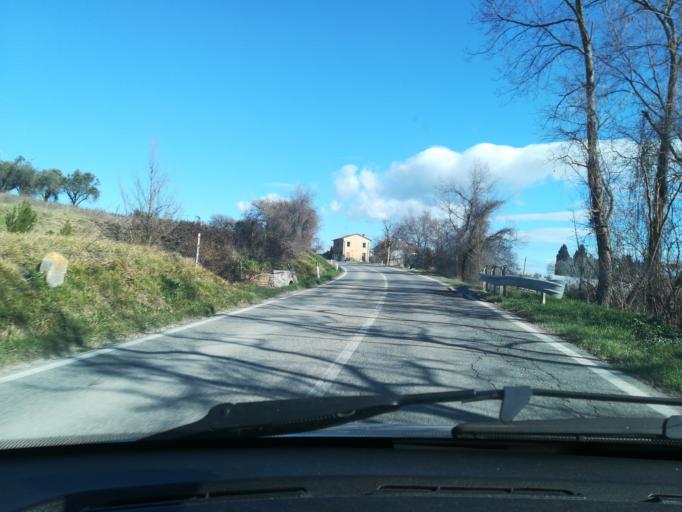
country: IT
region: The Marches
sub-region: Provincia di Macerata
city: Montecassiano
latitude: 43.3547
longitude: 13.4396
